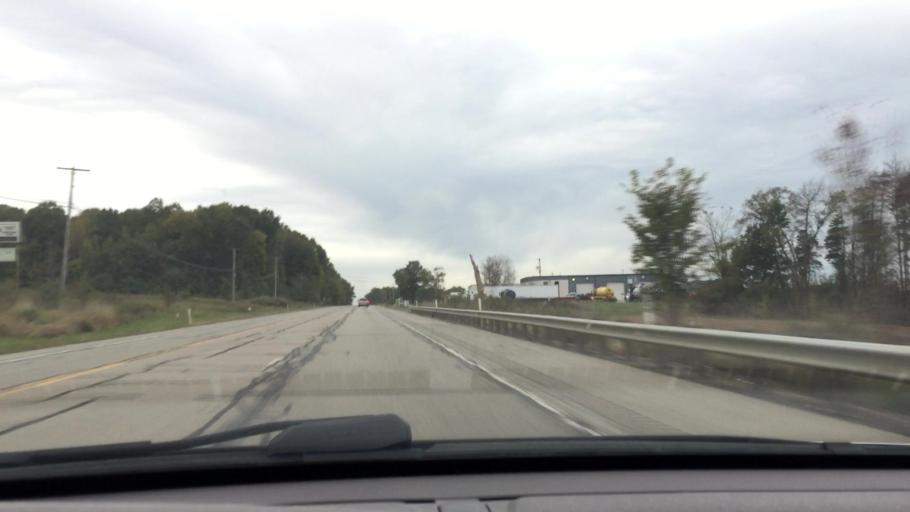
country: US
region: Pennsylvania
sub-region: Lawrence County
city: Oakwood
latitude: 41.0581
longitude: -80.4487
